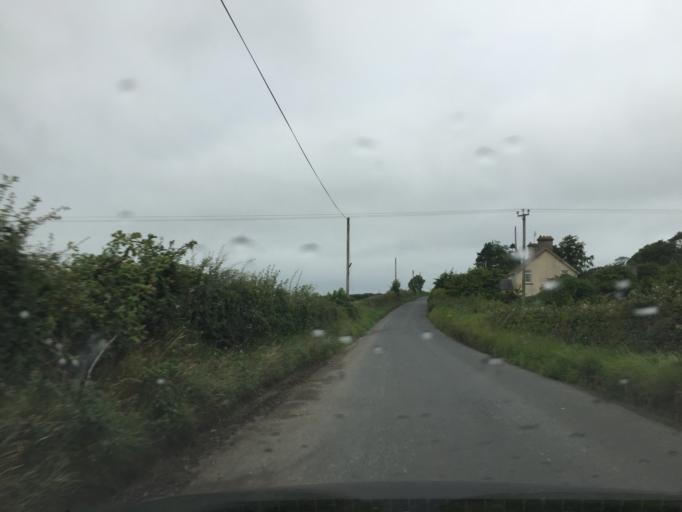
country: GB
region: Northern Ireland
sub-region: Down District
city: Kircubbin
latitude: 54.4919
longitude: -5.5121
